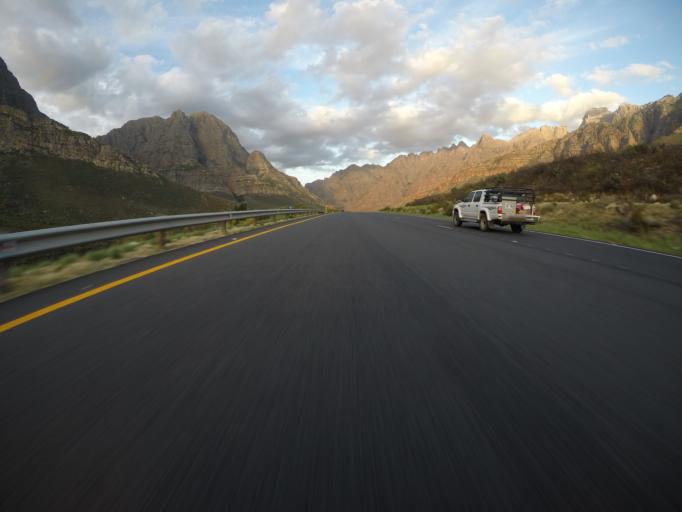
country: ZA
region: Western Cape
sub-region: Cape Winelands District Municipality
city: Paarl
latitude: -33.7248
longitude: 19.1458
